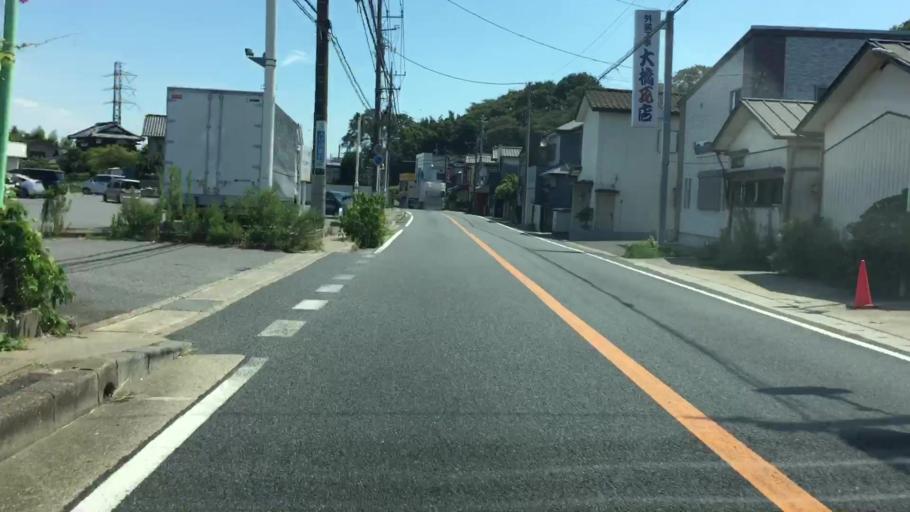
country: JP
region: Chiba
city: Matsudo
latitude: 35.7711
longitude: 139.9190
